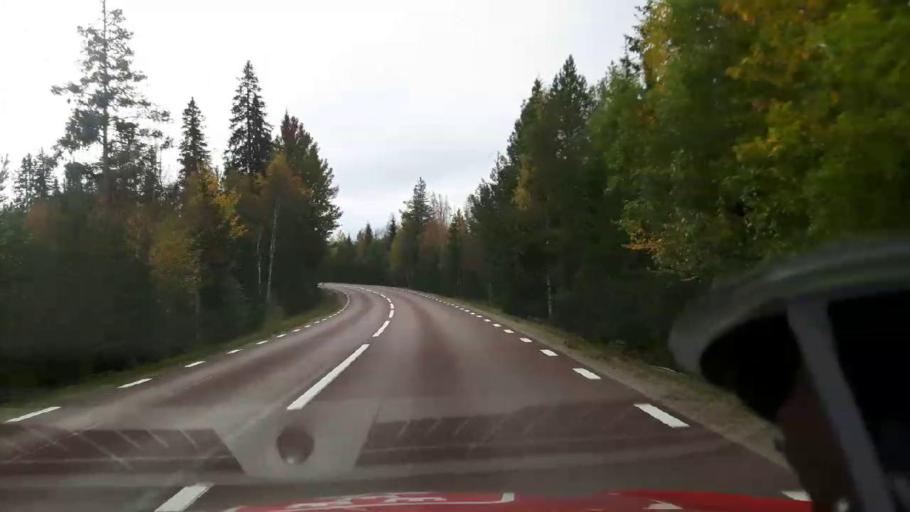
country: SE
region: Jaemtland
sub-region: Harjedalens Kommun
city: Sveg
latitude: 62.1900
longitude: 14.8619
